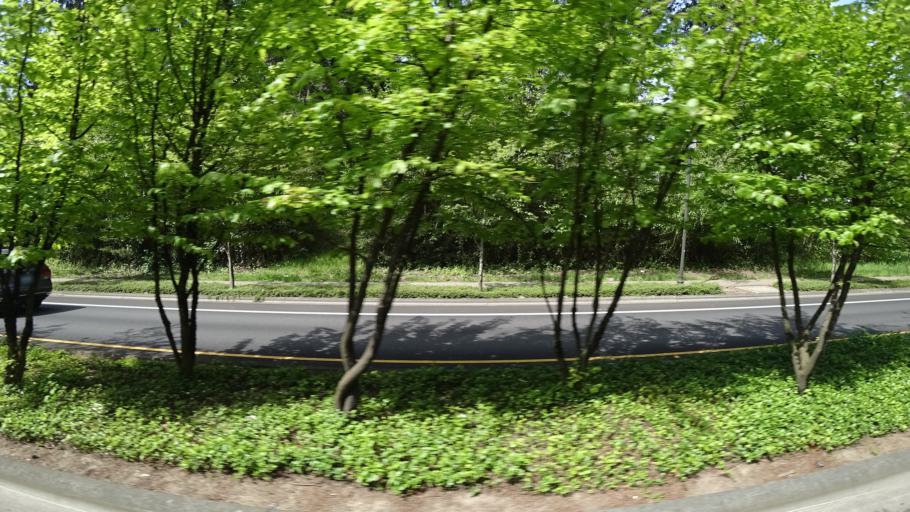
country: US
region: Oregon
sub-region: Washington County
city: Hillsboro
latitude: 45.5263
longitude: -122.9372
